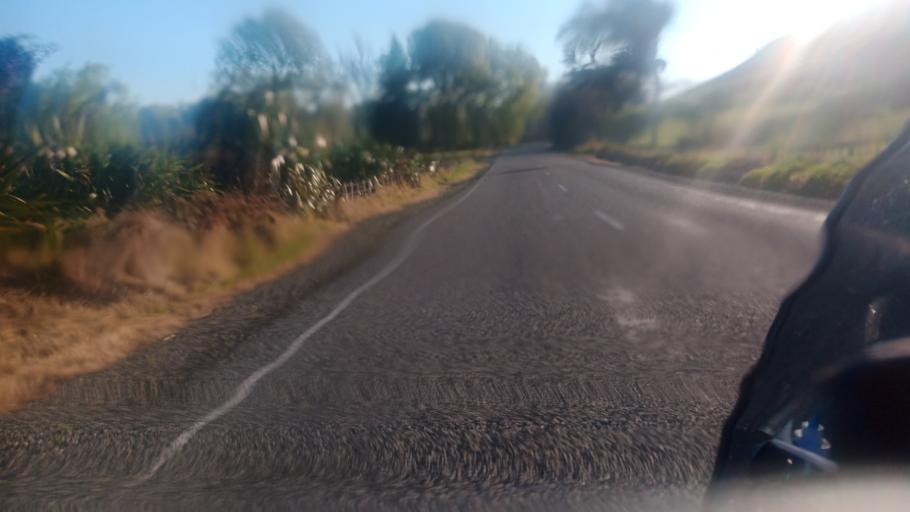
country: NZ
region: Hawke's Bay
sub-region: Wairoa District
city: Wairoa
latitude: -39.0478
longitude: 177.7617
